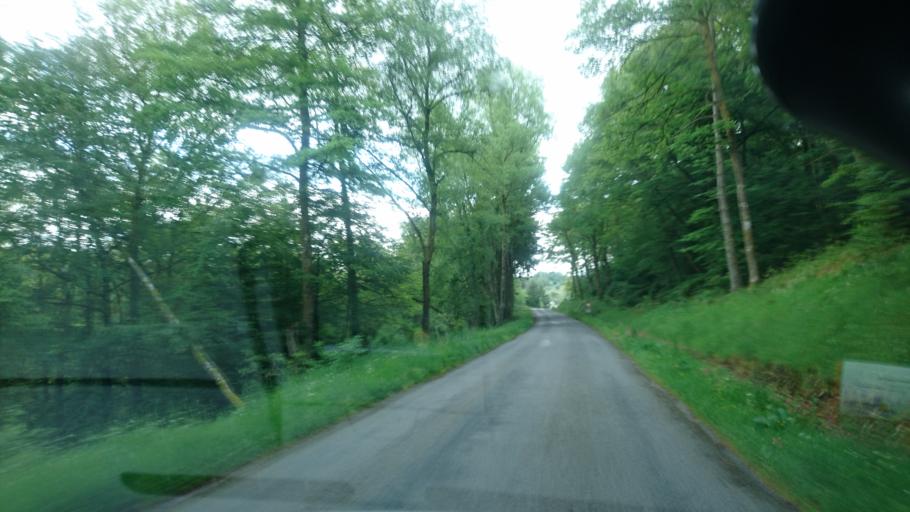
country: FR
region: Limousin
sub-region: Departement de la Haute-Vienne
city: Peyrat-le-Chateau
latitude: 45.7907
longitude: 1.9198
